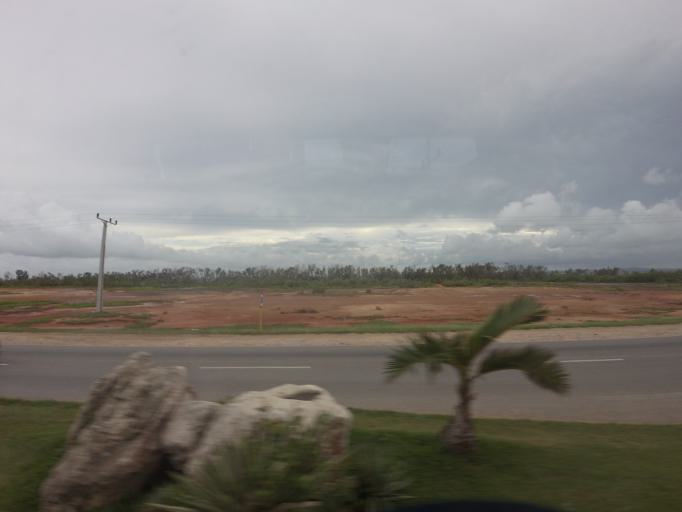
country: CU
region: Matanzas
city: Varadero
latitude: 23.1565
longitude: -81.2398
